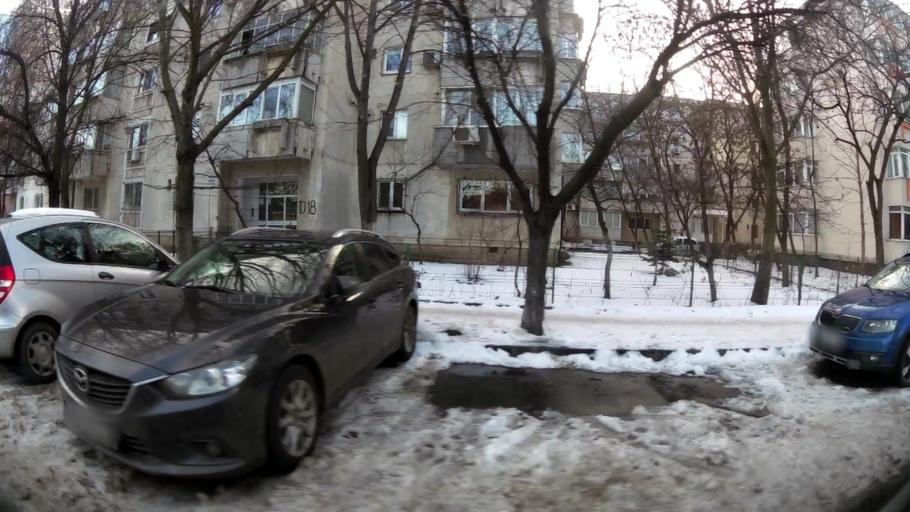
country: RO
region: Bucuresti
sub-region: Municipiul Bucuresti
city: Bucharest
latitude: 44.4241
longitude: 26.1326
